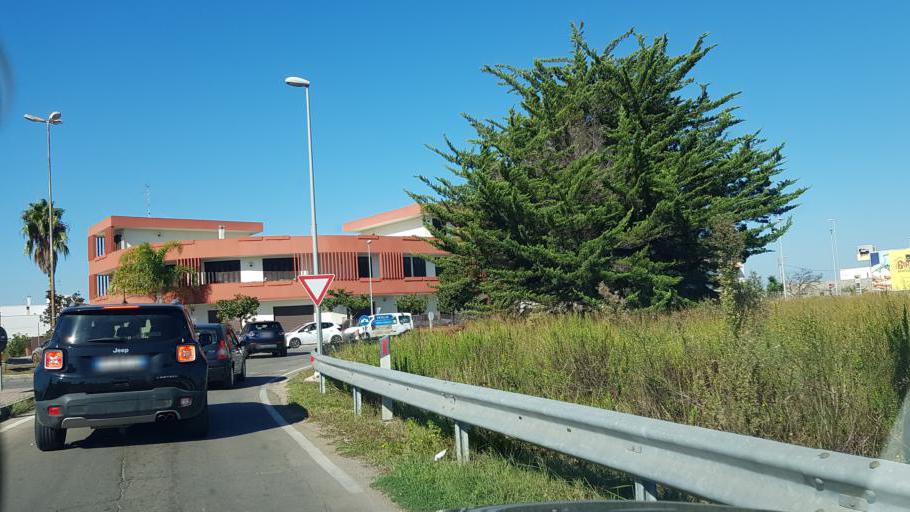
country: IT
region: Apulia
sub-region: Provincia di Lecce
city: Leverano
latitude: 40.2978
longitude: 17.9951
